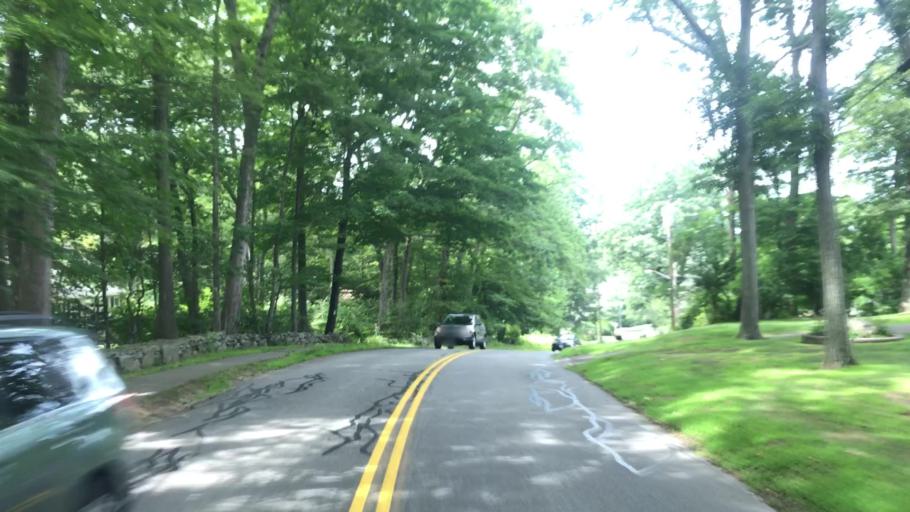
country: US
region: Connecticut
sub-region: New London County
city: Niantic
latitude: 41.3398
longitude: -72.2165
